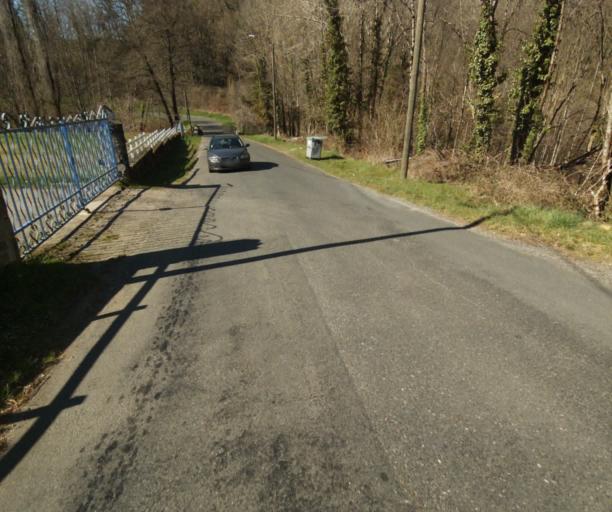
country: FR
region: Limousin
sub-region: Departement de la Correze
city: Tulle
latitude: 45.2739
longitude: 1.7380
